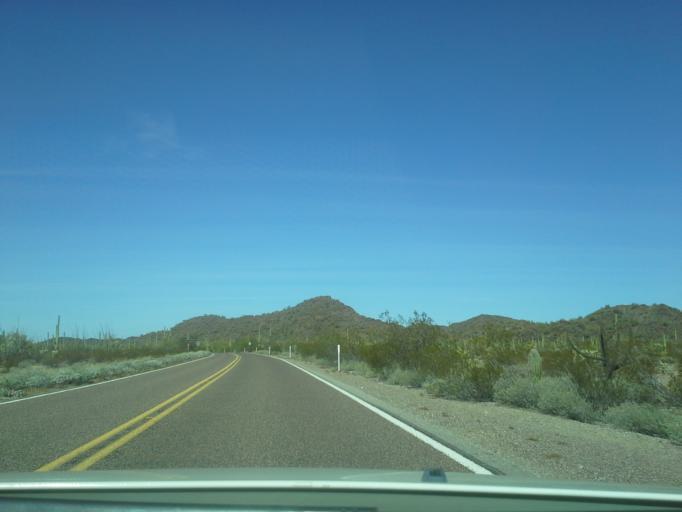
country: MX
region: Sonora
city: Sonoyta
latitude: 31.9607
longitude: -112.8005
